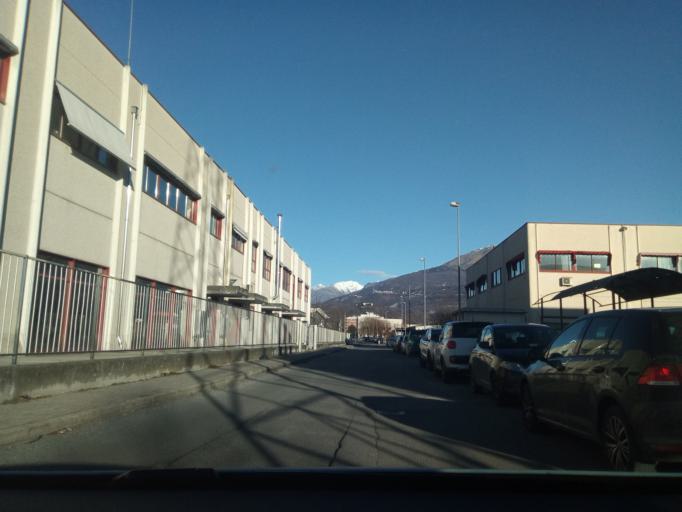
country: IT
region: Piedmont
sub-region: Provincia di Torino
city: Cascinette d'Ivrea
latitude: 45.4685
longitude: 7.9069
